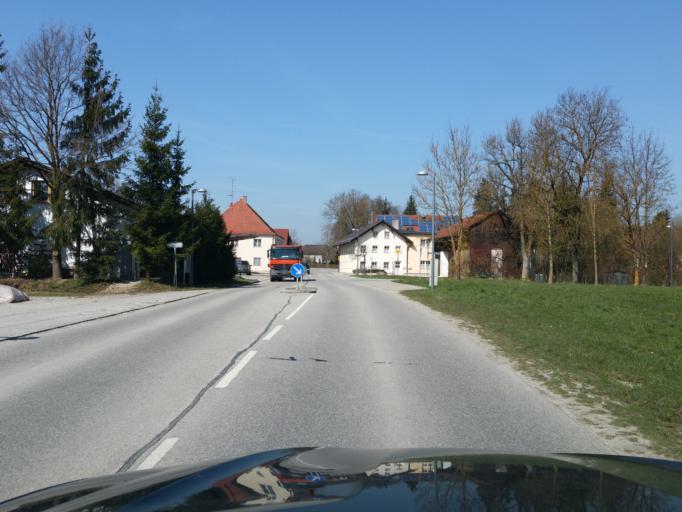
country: DE
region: Bavaria
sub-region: Lower Bavaria
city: Vilsheim
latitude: 48.4468
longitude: 12.1078
